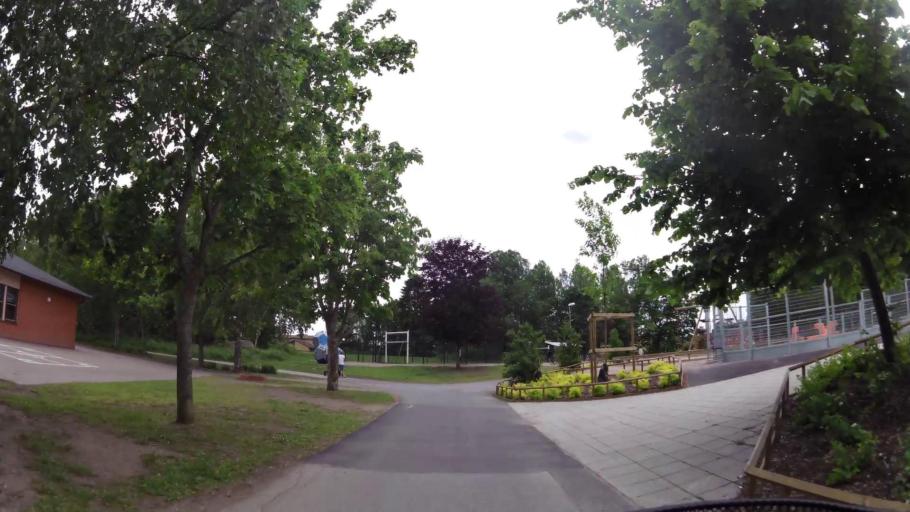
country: SE
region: OEstergoetland
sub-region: Linkopings Kommun
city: Linkoping
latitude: 58.3857
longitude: 15.5692
